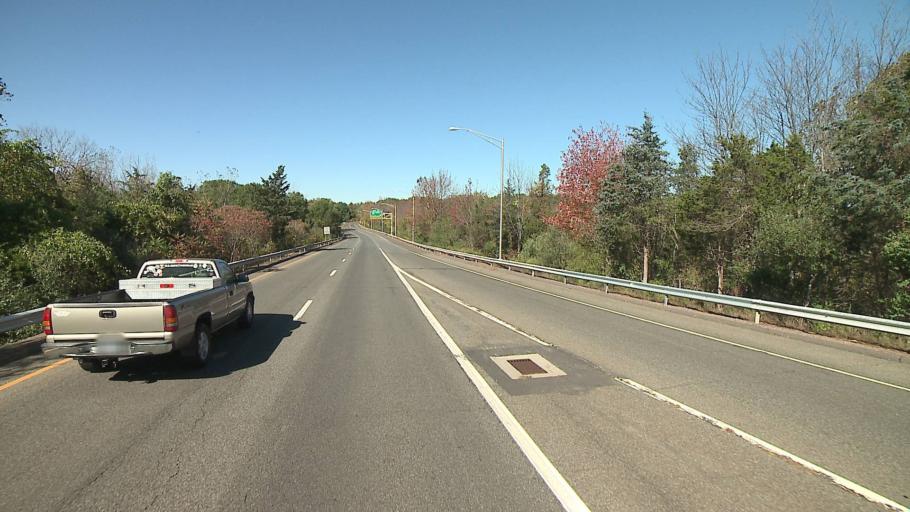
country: US
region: Connecticut
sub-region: New Haven County
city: Meriden
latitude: 41.5350
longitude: -72.7562
